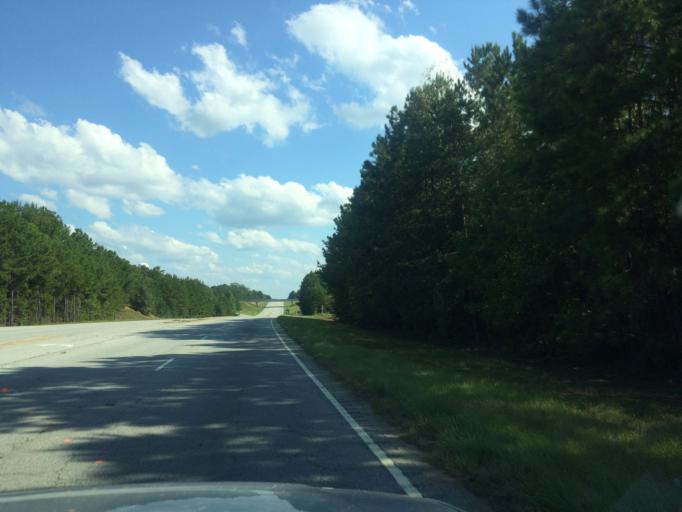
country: US
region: South Carolina
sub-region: Greenwood County
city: Ware Shoals
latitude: 34.4312
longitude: -82.2406
